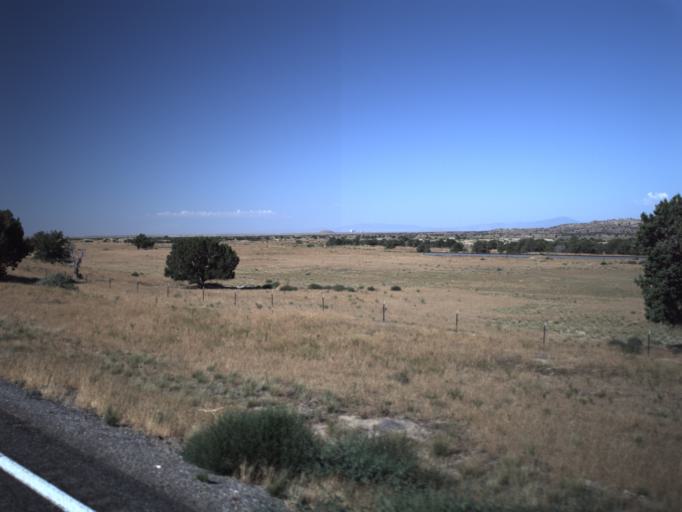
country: US
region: Utah
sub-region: Millard County
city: Delta
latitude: 39.6289
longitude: -112.3105
